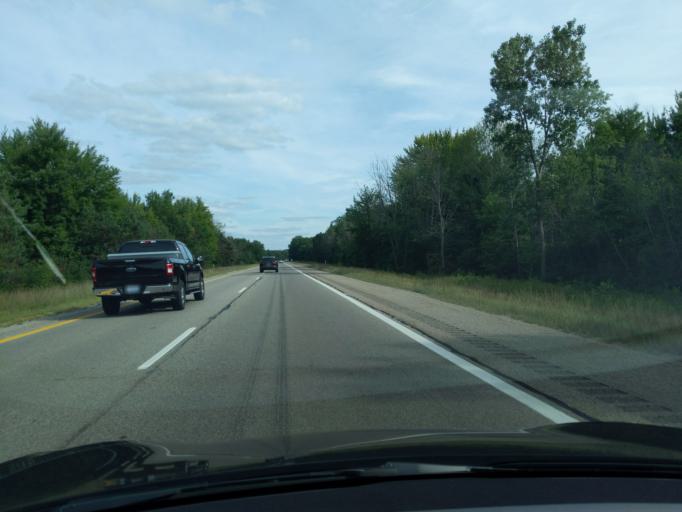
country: US
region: Michigan
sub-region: Muskegon County
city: Fruitport
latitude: 43.0975
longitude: -86.1056
